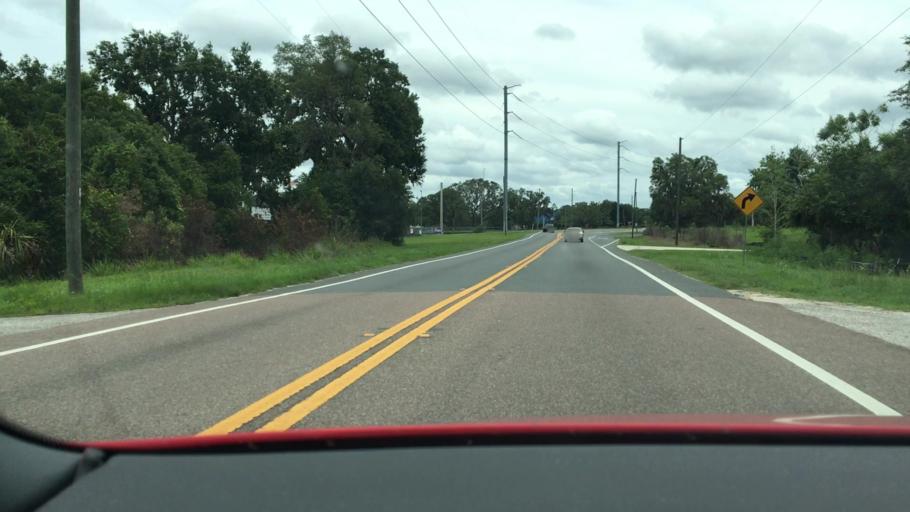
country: US
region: Florida
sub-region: Lake County
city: Eustis
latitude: 28.8753
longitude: -81.6731
